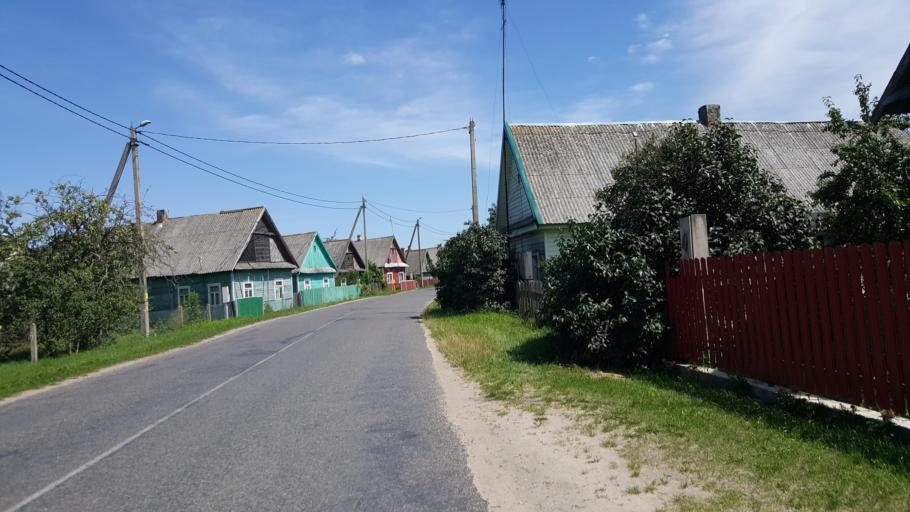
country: BY
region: Brest
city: Pruzhany
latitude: 52.5627
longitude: 24.2203
